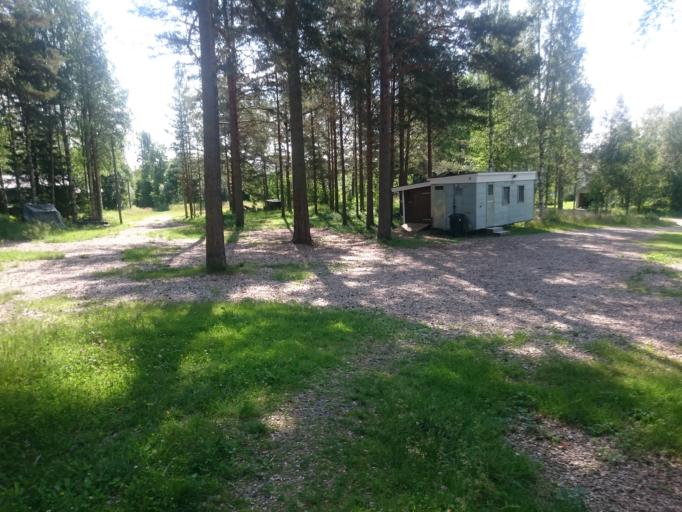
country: SE
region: Vaesternorrland
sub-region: OErnskoeldsviks Kommun
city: Bredbyn
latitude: 63.3019
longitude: 18.2592
